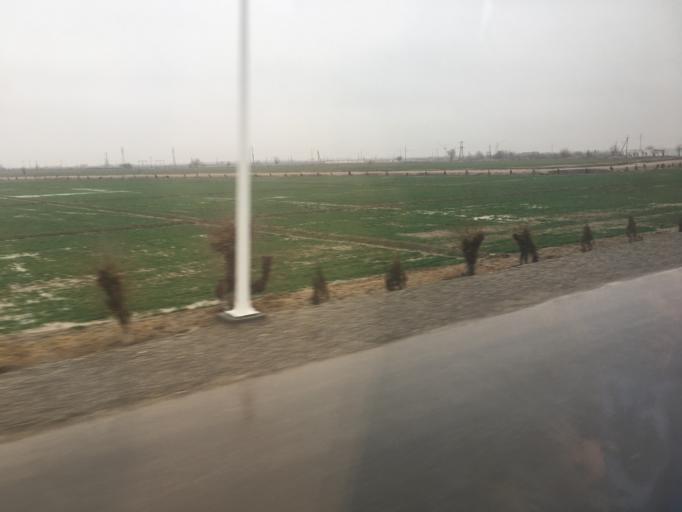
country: TM
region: Lebap
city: Turkmenabat
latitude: 38.9966
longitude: 63.5864
